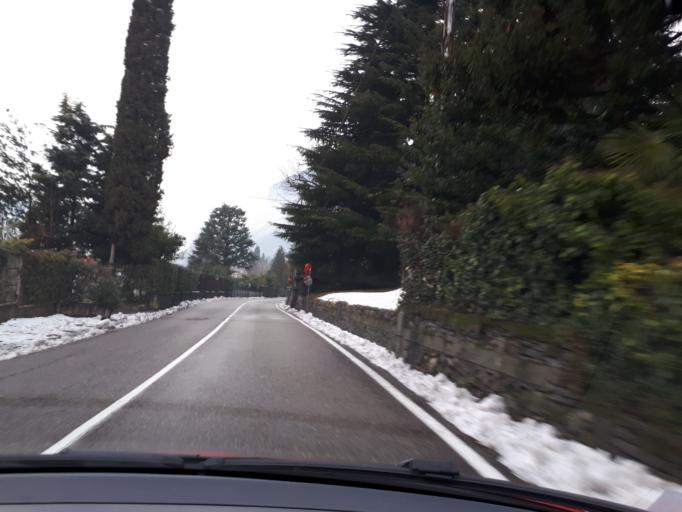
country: IT
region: Lombardy
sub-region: Provincia di Lecco
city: Lierna
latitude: 45.9545
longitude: 9.3019
